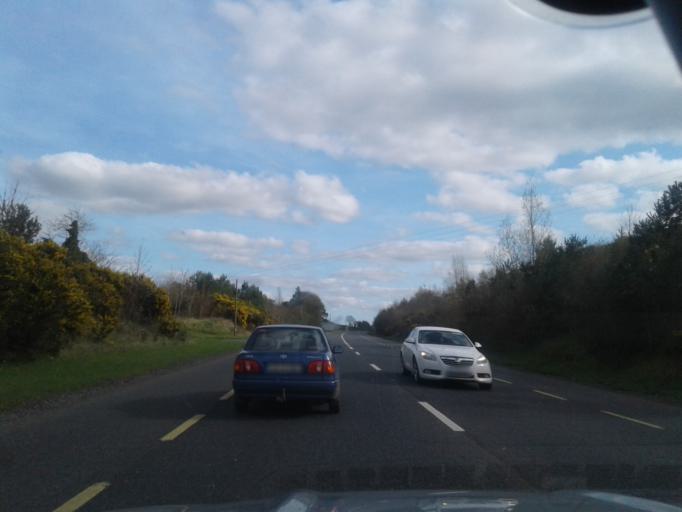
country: IE
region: Ulster
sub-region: County Monaghan
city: Carrickmacross
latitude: 53.9376
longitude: -6.6577
